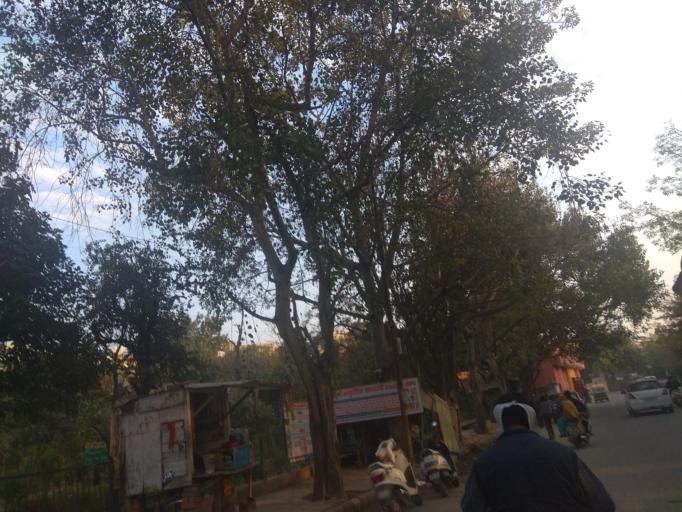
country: IN
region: NCT
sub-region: West Delhi
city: Nangloi Jat
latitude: 28.6354
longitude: 77.0655
